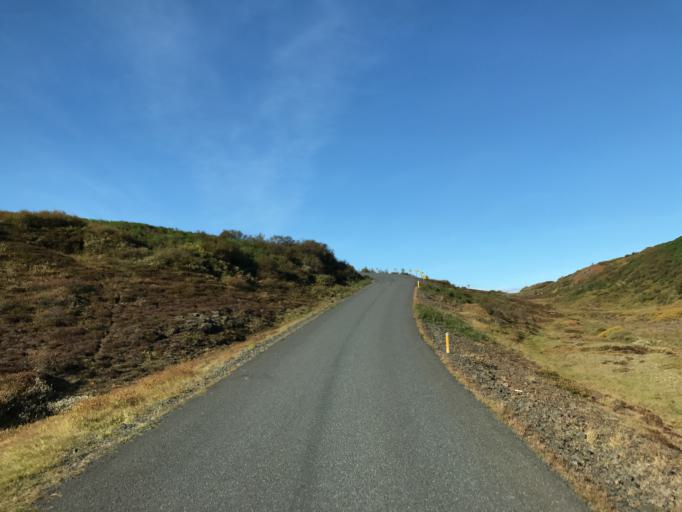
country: IS
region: South
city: Hveragerdi
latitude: 64.1392
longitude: -21.2566
